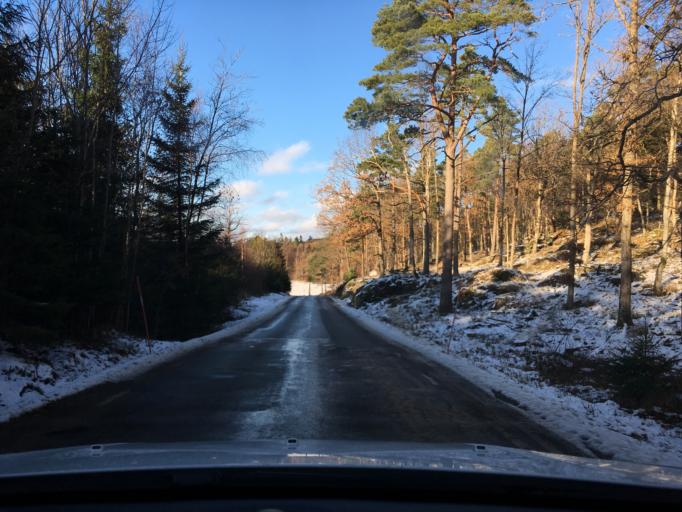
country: SE
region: Vaestra Goetaland
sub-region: Tjorns Kommun
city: Myggenas
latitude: 58.0958
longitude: 11.7168
